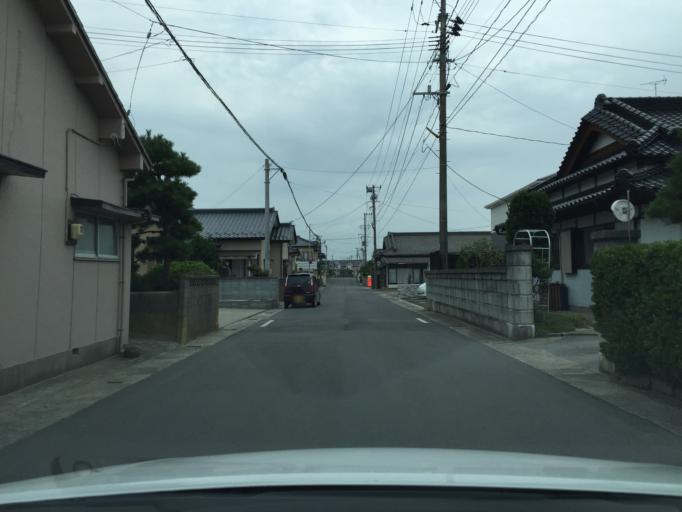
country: JP
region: Fukushima
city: Iwaki
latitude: 37.0133
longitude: 140.9713
